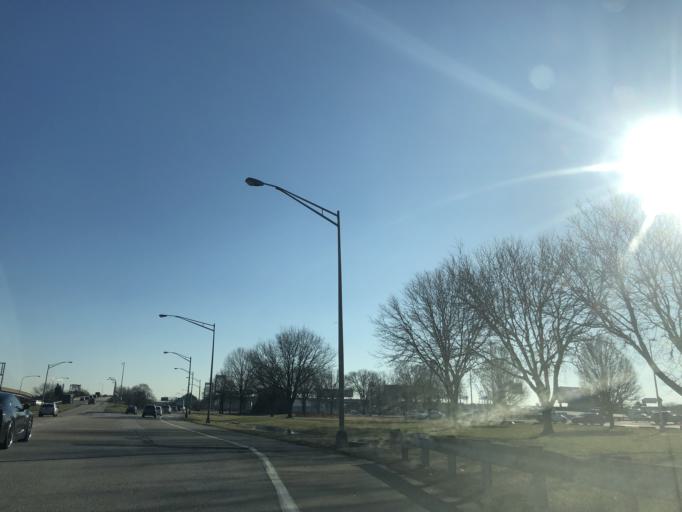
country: US
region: New Jersey
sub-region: Camden County
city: Camden
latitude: 39.9111
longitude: -75.1559
